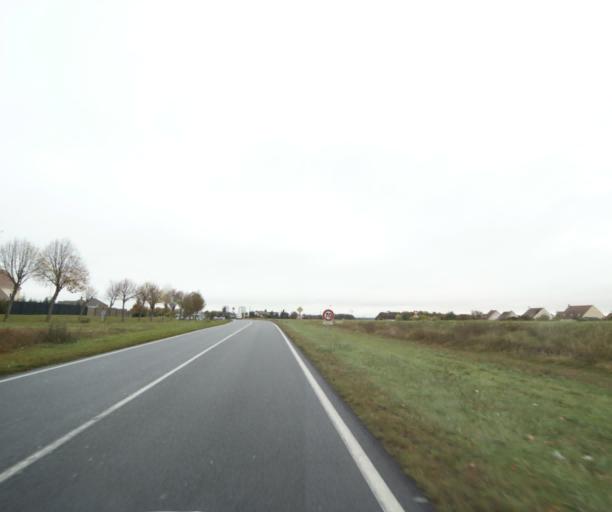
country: FR
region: Centre
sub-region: Departement d'Eure-et-Loir
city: Luray
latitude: 48.7288
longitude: 1.3894
